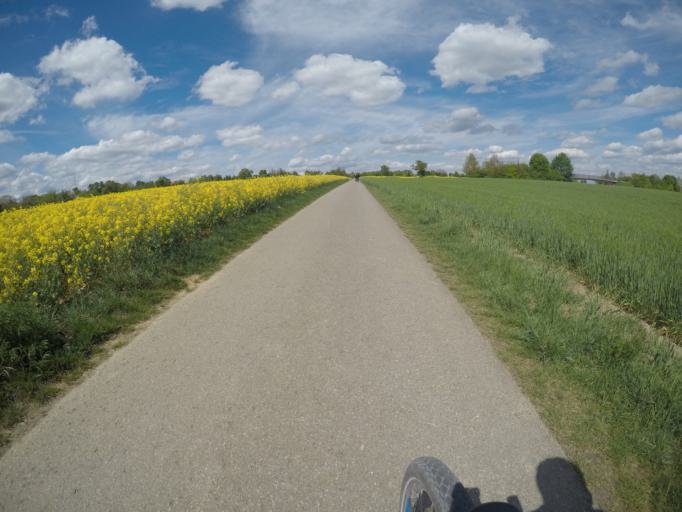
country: DE
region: Baden-Wuerttemberg
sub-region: Regierungsbezirk Stuttgart
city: Nufringen
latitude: 48.6396
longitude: 8.8806
